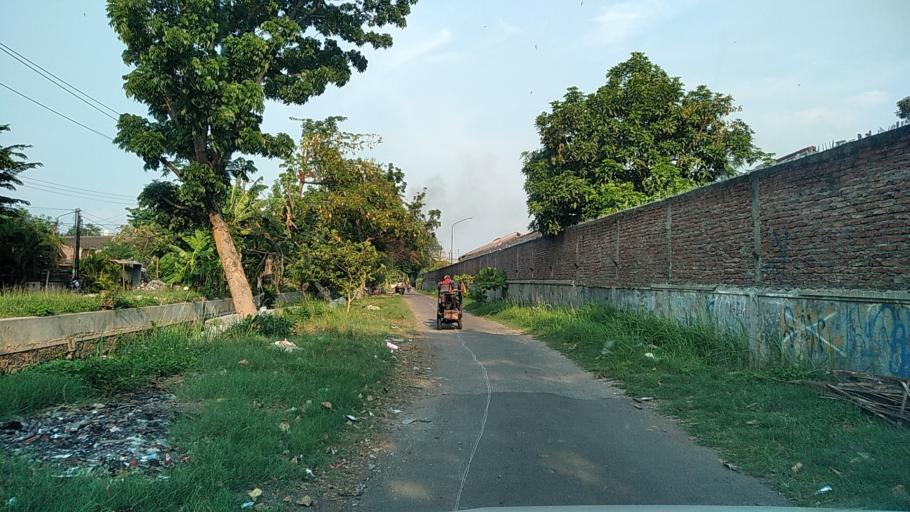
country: ID
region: Central Java
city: Semarang
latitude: -6.9659
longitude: 110.4017
